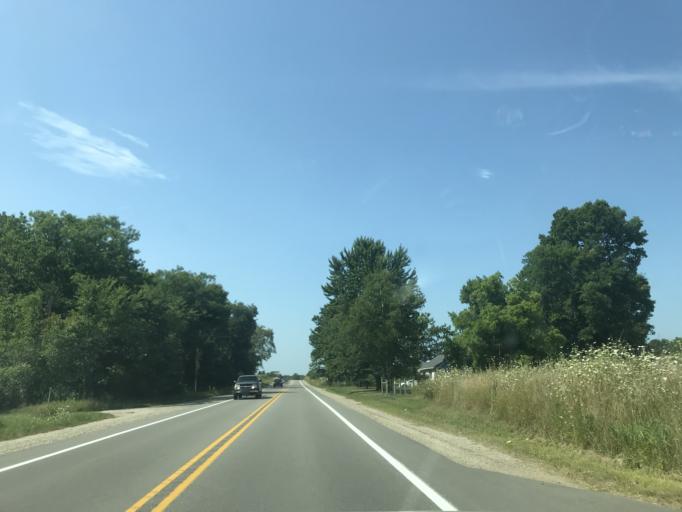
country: US
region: Michigan
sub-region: Newaygo County
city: Newaygo
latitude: 43.3567
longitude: -85.8042
